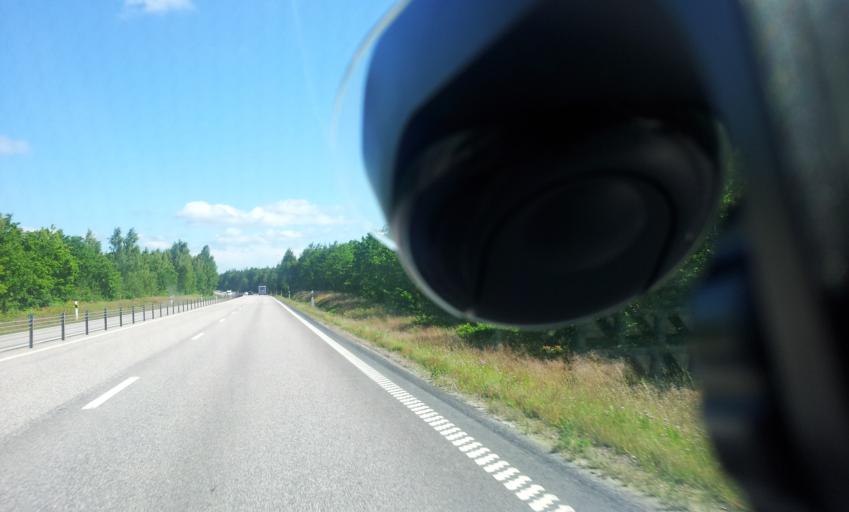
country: SE
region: Kalmar
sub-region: Monsteras Kommun
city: Timmernabben
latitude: 56.9882
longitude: 16.4087
